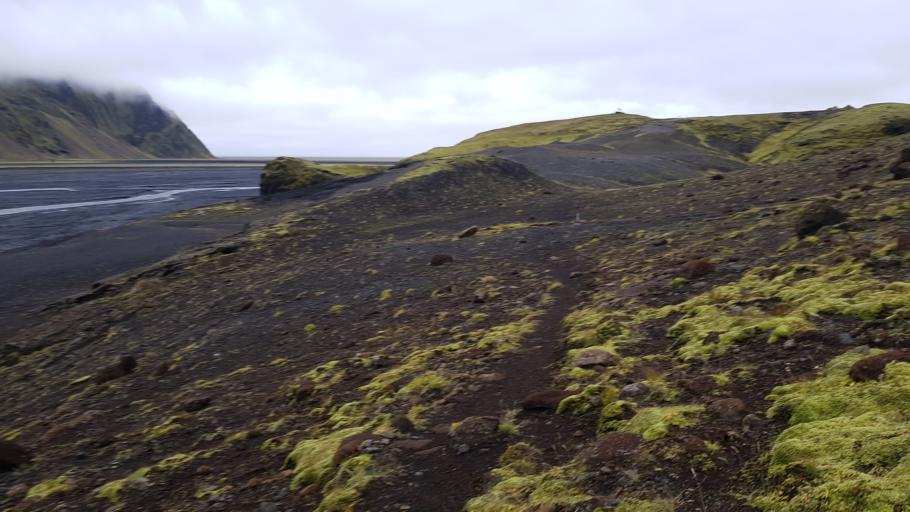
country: IS
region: South
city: Vestmannaeyjar
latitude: 63.5294
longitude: -18.8484
